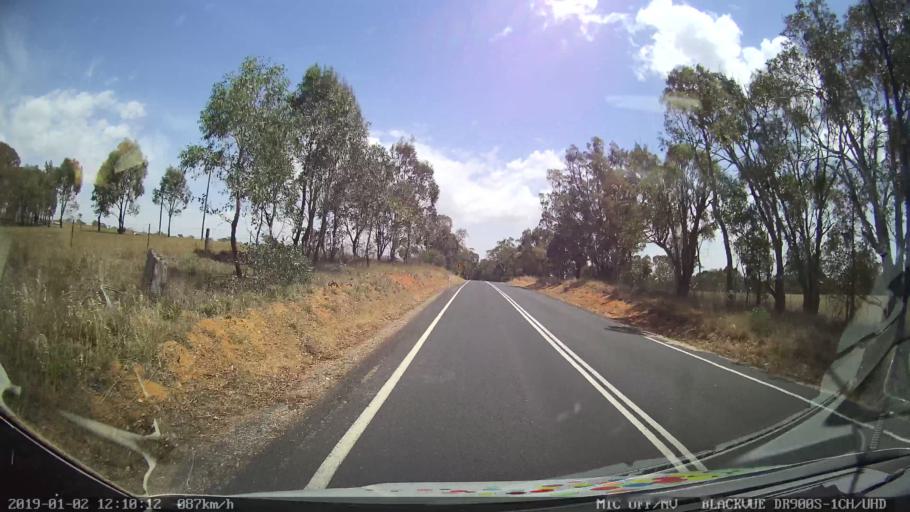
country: AU
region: New South Wales
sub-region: Young
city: Young
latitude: -34.4631
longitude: 148.2652
